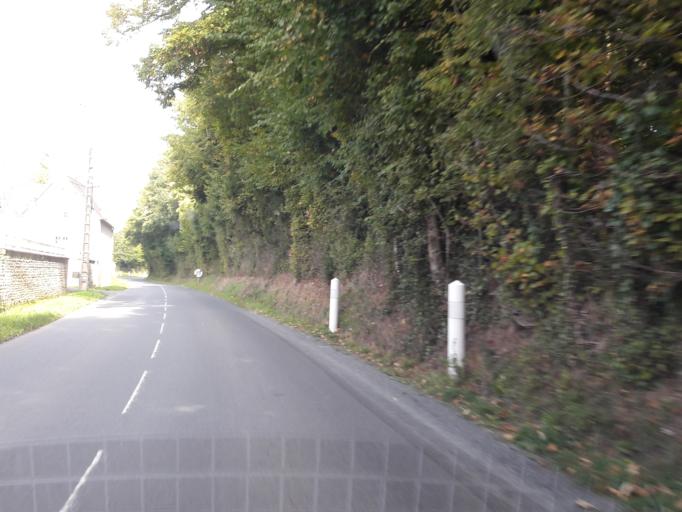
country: FR
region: Lower Normandy
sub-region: Departement du Calvados
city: Bayeux
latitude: 49.2188
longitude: -0.7099
